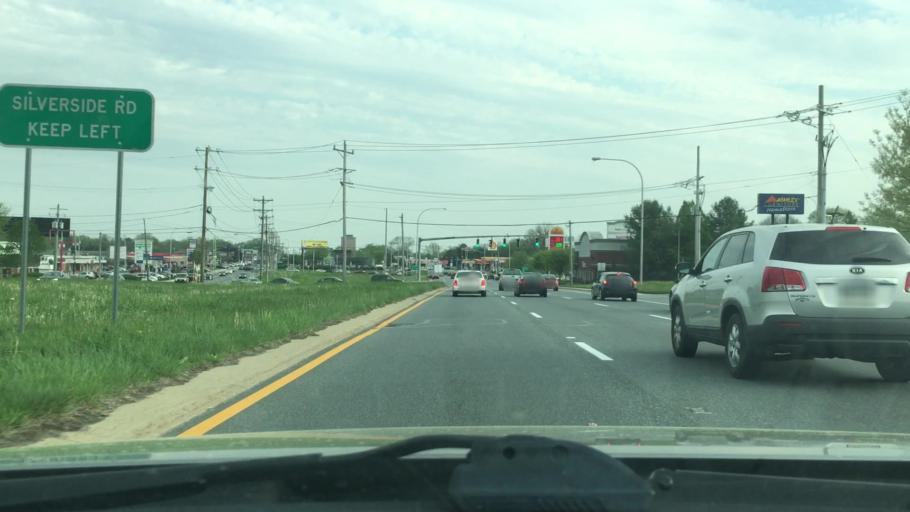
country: US
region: Delaware
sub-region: New Castle County
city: Greenville
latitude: 39.8123
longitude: -75.5500
